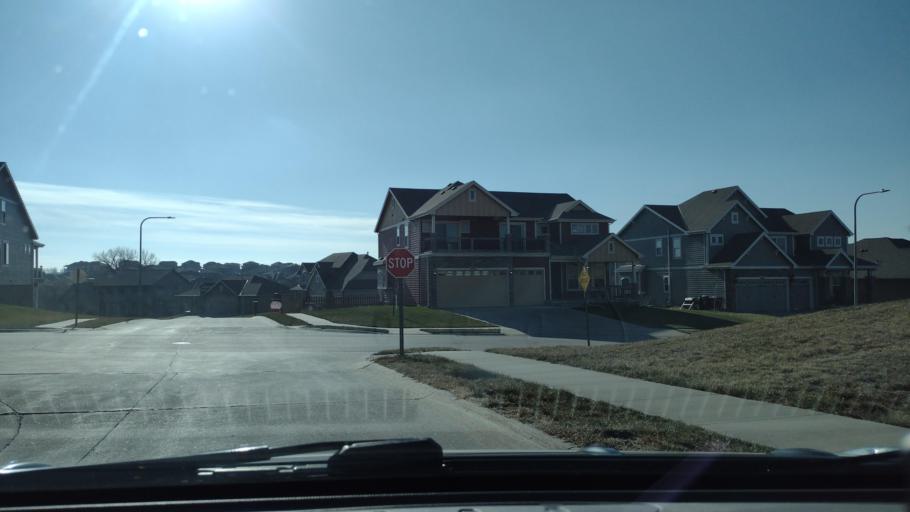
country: US
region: Nebraska
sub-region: Sarpy County
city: La Vista
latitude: 41.1690
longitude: -96.0160
